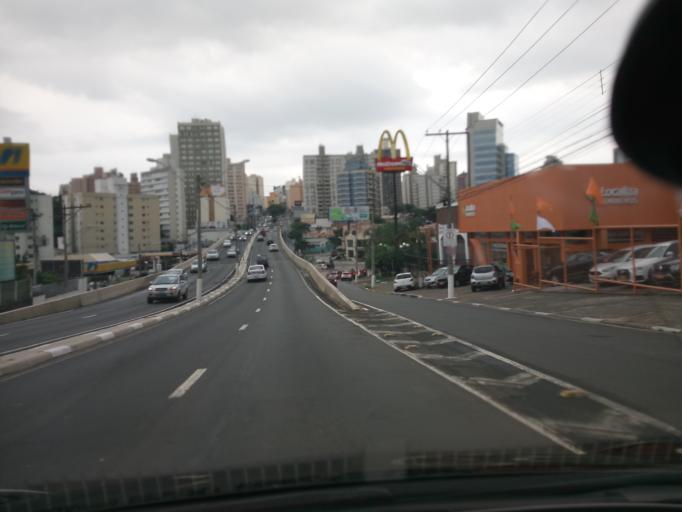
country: BR
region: Sao Paulo
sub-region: Campinas
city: Campinas
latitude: -22.9061
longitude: -47.0449
